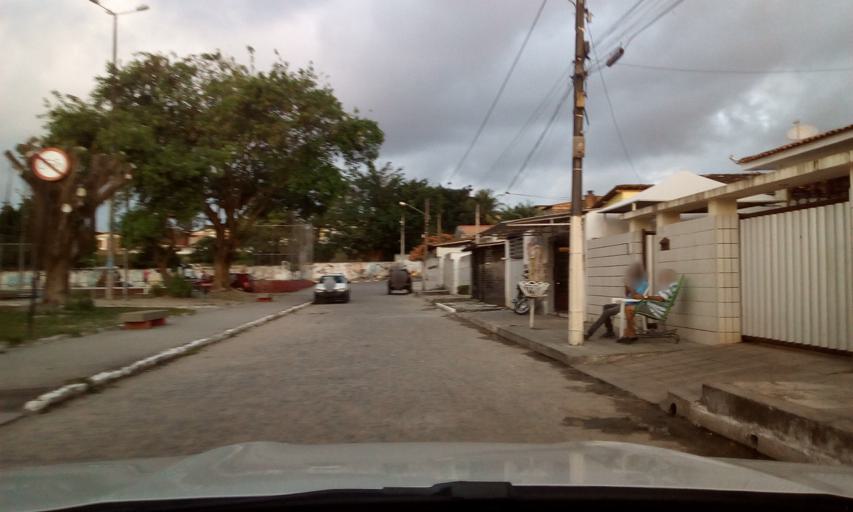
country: BR
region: Paraiba
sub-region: Joao Pessoa
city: Joao Pessoa
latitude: -7.1777
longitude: -34.8837
